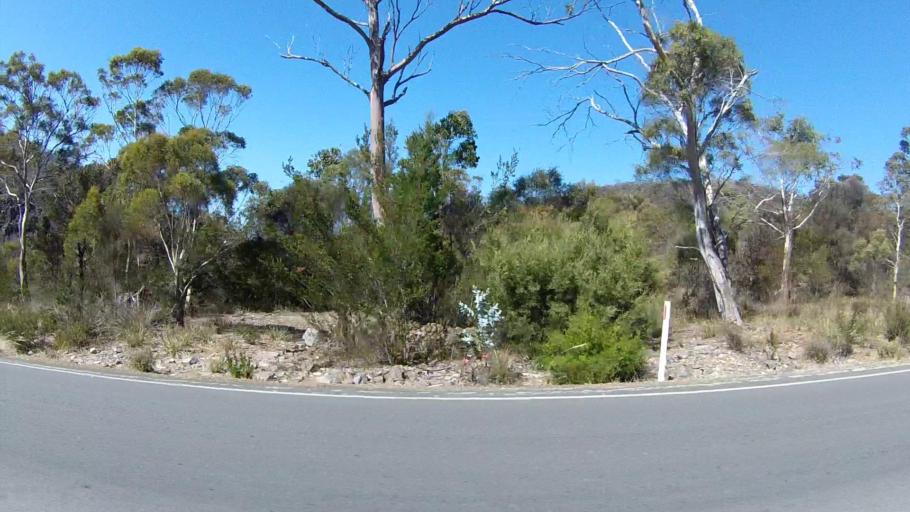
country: AU
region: Tasmania
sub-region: Sorell
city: Sorell
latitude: -42.5592
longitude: 147.8479
